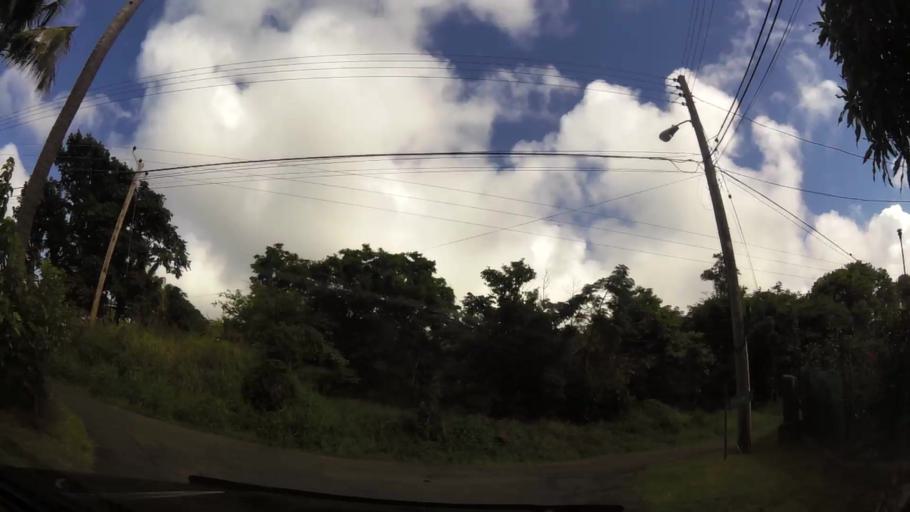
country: MS
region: Saint Peter
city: Saint Peters
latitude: 16.7517
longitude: -62.2219
